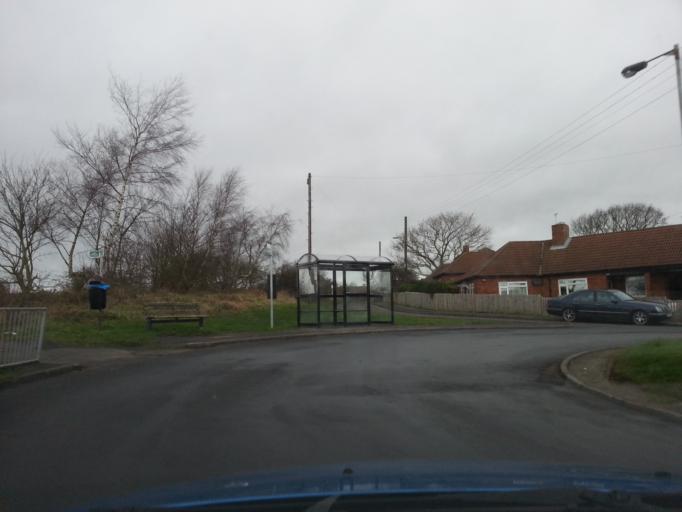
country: GB
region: England
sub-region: County Durham
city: Crook
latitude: 54.7276
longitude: -1.7603
